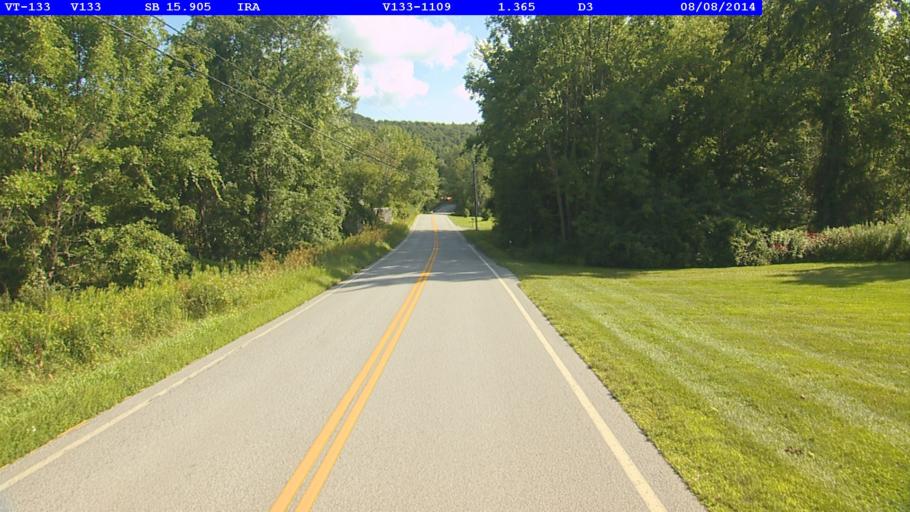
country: US
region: Vermont
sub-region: Rutland County
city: West Rutland
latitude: 43.5136
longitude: -73.0734
